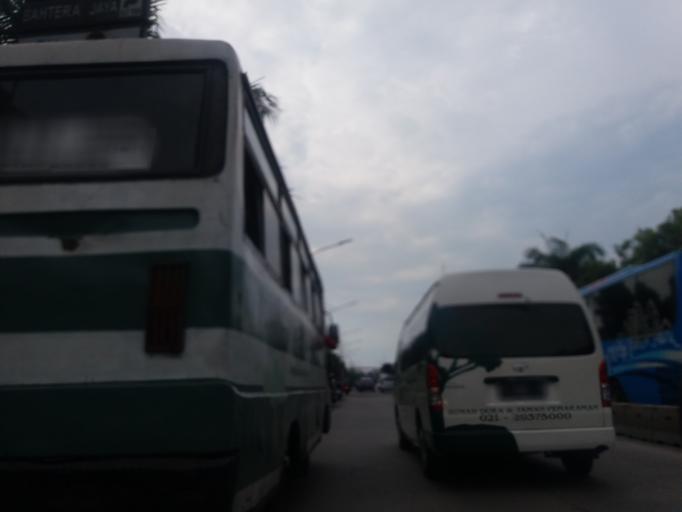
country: ID
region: Jakarta Raya
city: Jakarta
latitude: -6.1367
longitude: 106.8322
